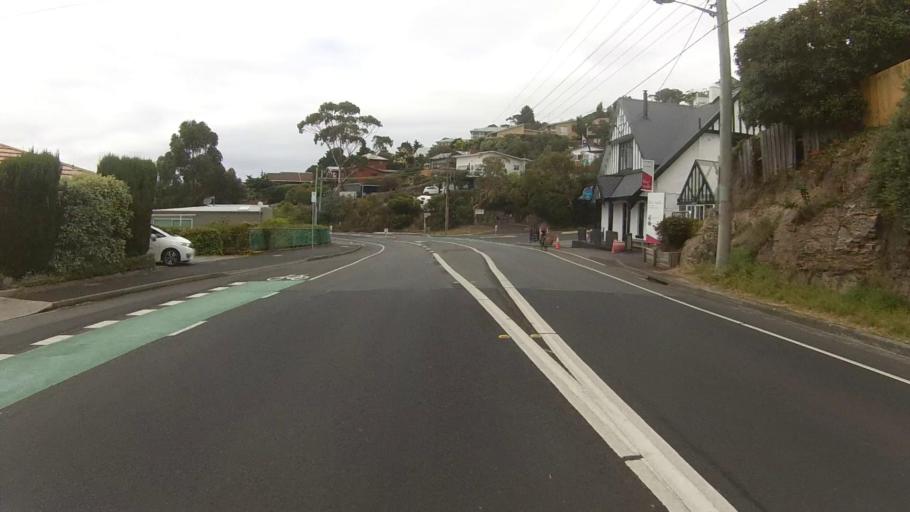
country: AU
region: Tasmania
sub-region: Kingborough
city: Taroona
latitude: -42.9240
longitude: 147.3603
